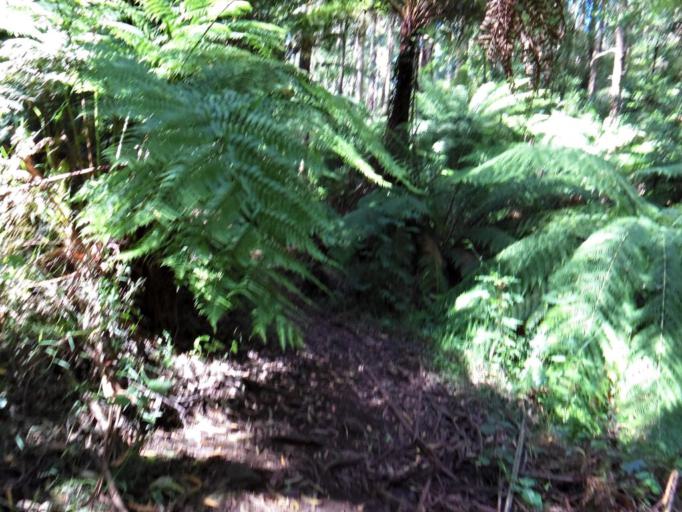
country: AU
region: Victoria
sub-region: Yarra Ranges
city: Mount Dandenong
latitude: -37.8303
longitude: 145.3645
